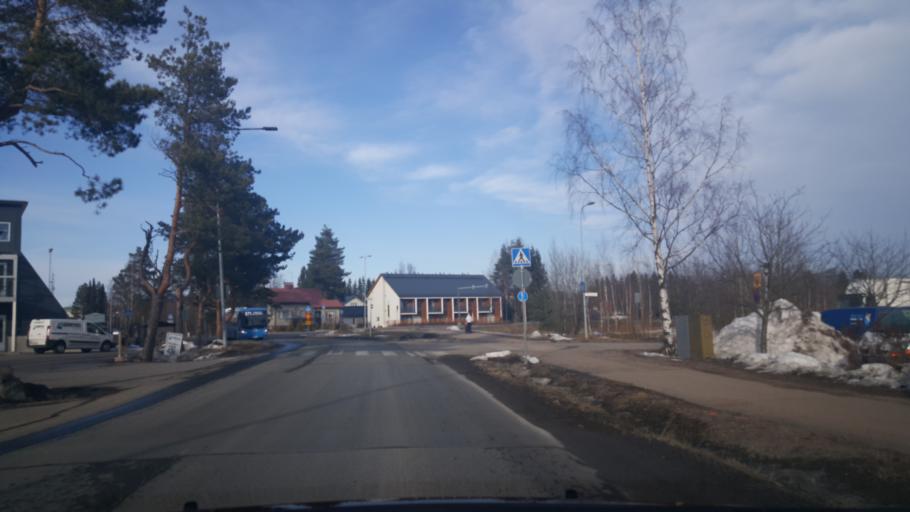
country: FI
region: Uusimaa
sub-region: Helsinki
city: Vantaa
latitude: 60.2913
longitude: 25.0091
